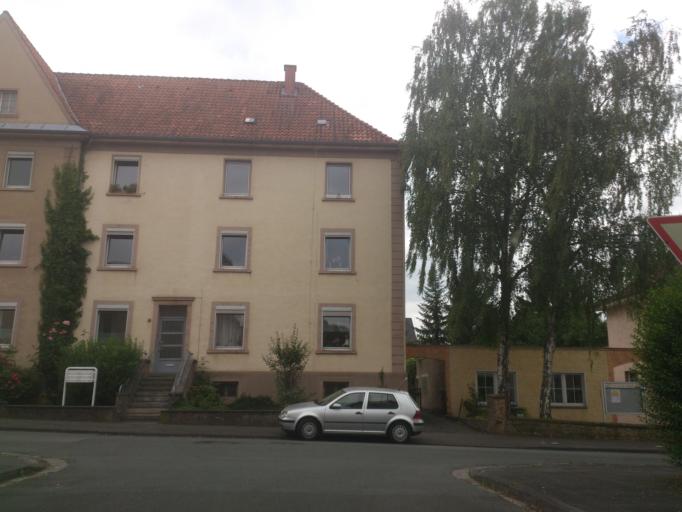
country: DE
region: North Rhine-Westphalia
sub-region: Regierungsbezirk Detmold
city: Paderborn
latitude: 51.7104
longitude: 8.7494
